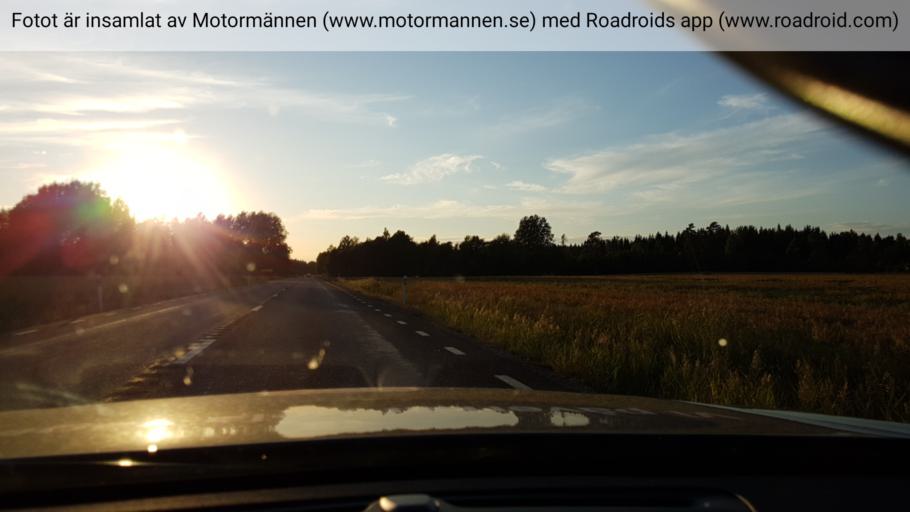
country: SE
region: Vaermland
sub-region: Storfors Kommun
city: Storfors
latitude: 59.4628
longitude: 14.3502
